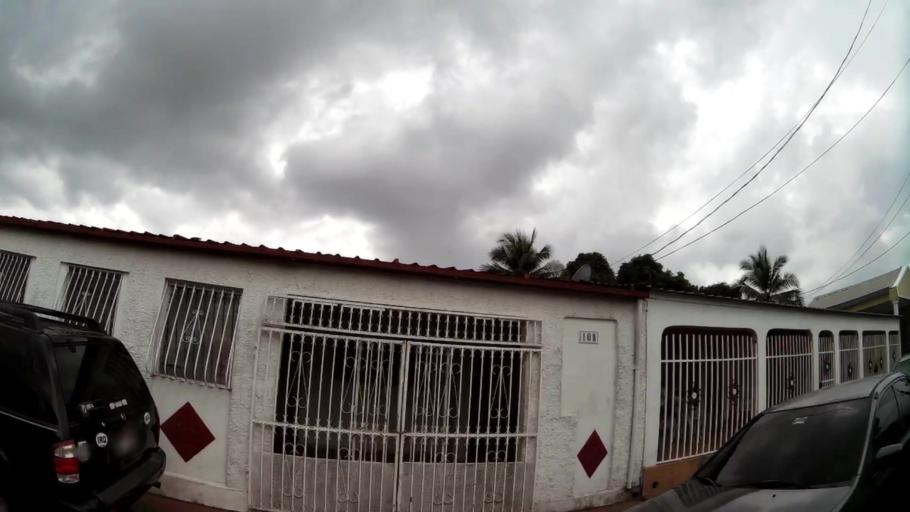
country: PA
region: Panama
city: Tocumen
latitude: 9.0608
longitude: -79.4131
